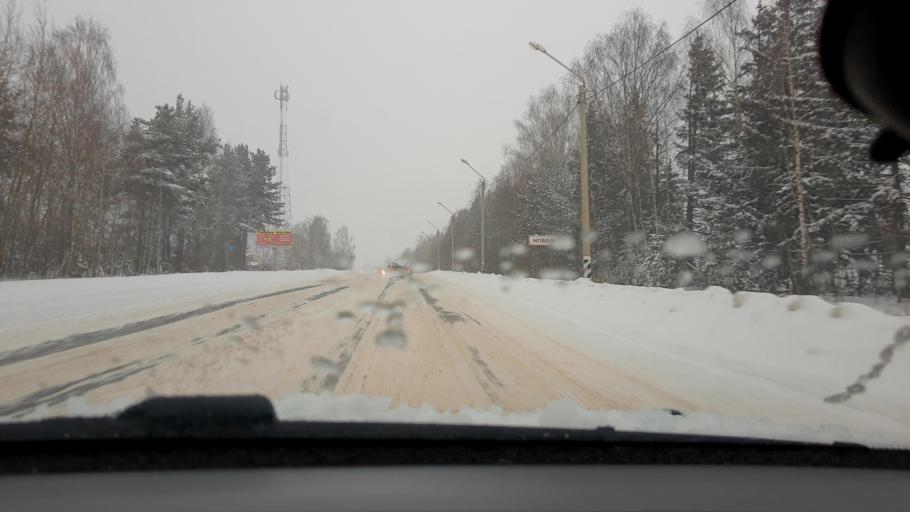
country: RU
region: Nizjnij Novgorod
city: Purekh
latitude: 56.6593
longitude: 43.0960
